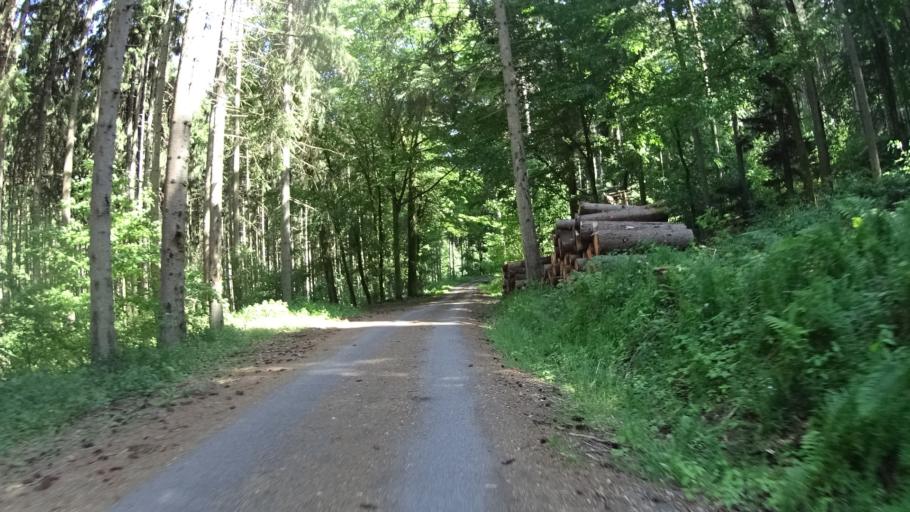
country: DE
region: Baden-Wuerttemberg
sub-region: Karlsruhe Region
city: Hopfingen
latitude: 49.6307
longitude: 9.4415
